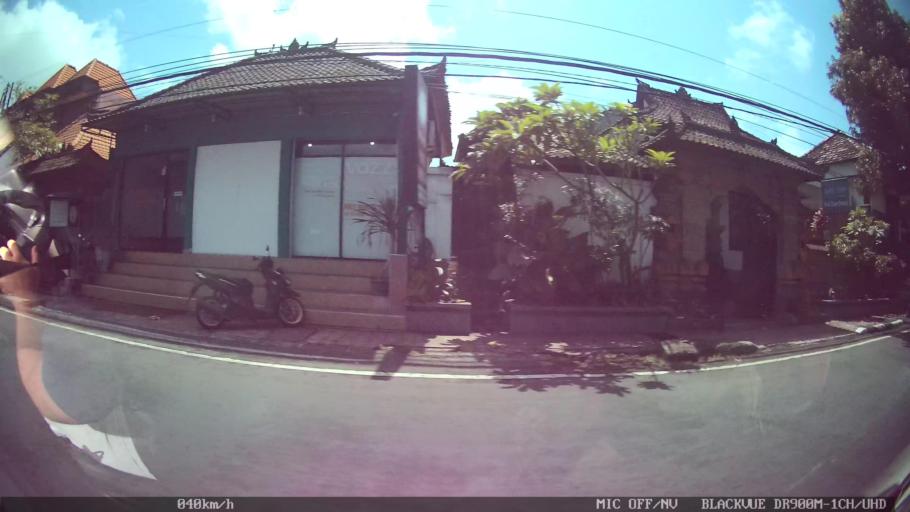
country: ID
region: Bali
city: Banjar Jabejero
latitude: -8.6005
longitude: 115.2721
